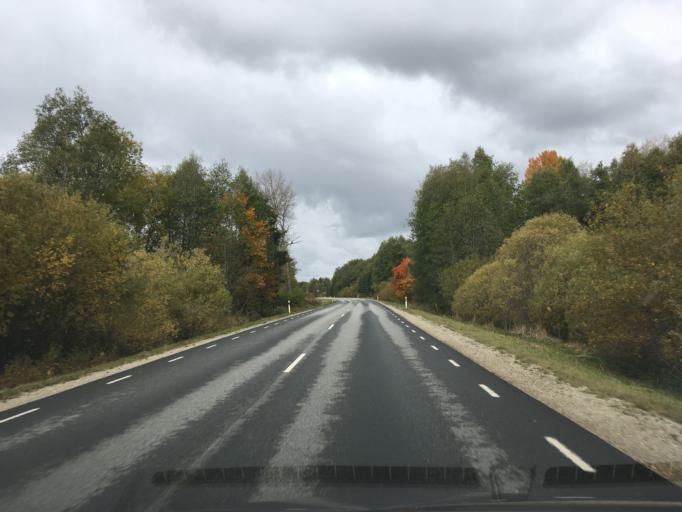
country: EE
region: Harju
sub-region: Anija vald
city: Kehra
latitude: 59.3032
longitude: 25.3588
